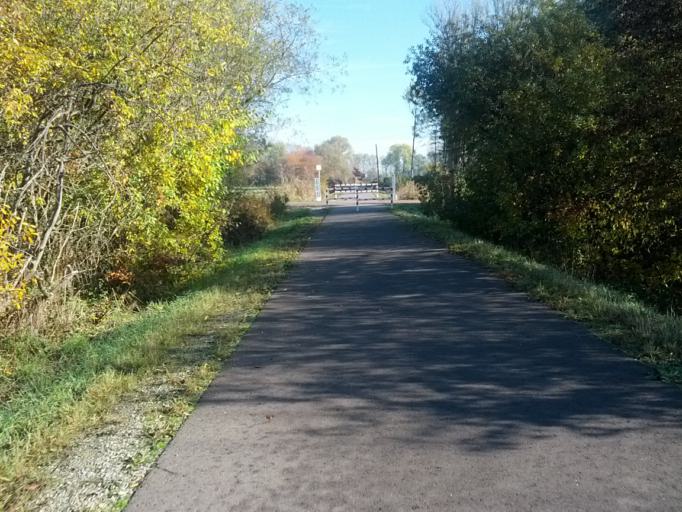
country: DE
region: Thuringia
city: Sonneborn
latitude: 50.9949
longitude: 10.5691
